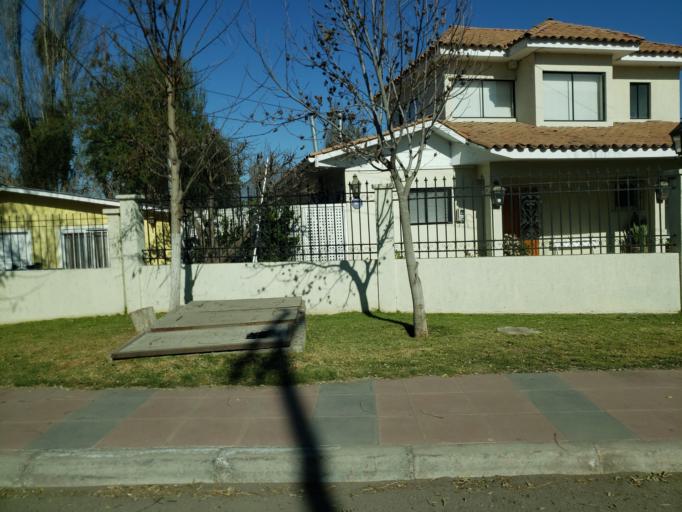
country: CL
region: Santiago Metropolitan
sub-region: Provincia de Talagante
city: El Monte
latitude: -33.6798
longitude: -70.9777
